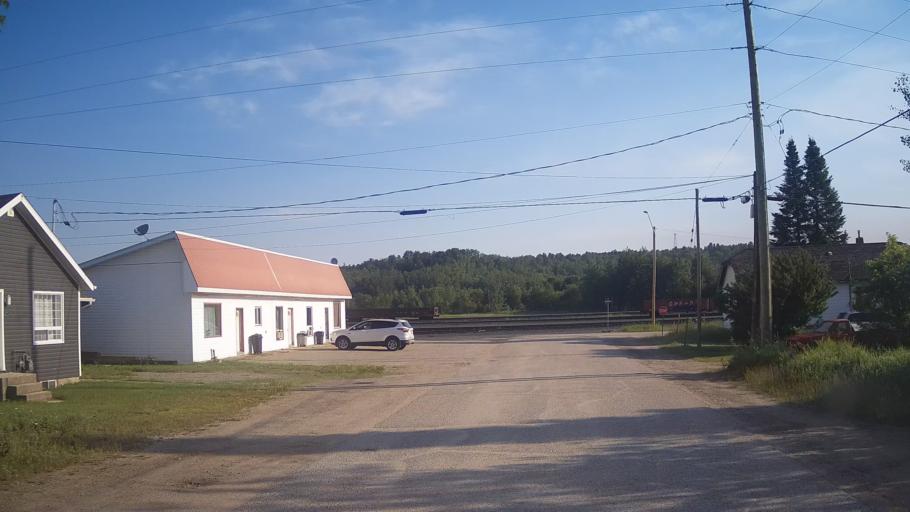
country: CA
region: Ontario
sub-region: Rainy River District
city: Atikokan
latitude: 49.4187
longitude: -91.6673
